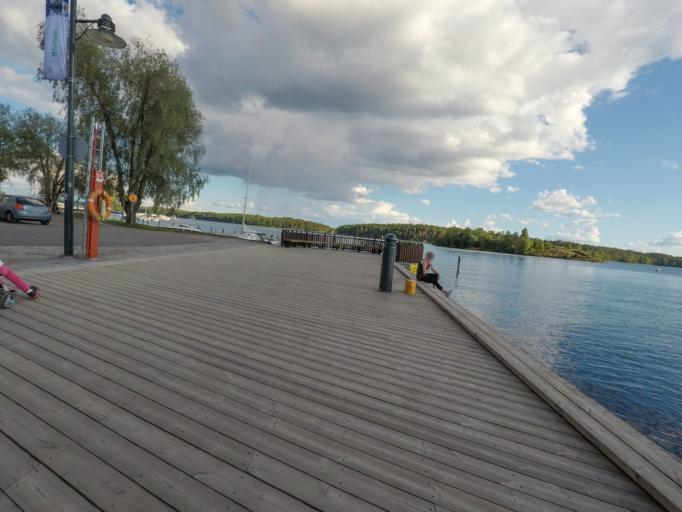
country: FI
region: Southern Savonia
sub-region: Savonlinna
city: Savonlinna
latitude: 61.8655
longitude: 28.8866
